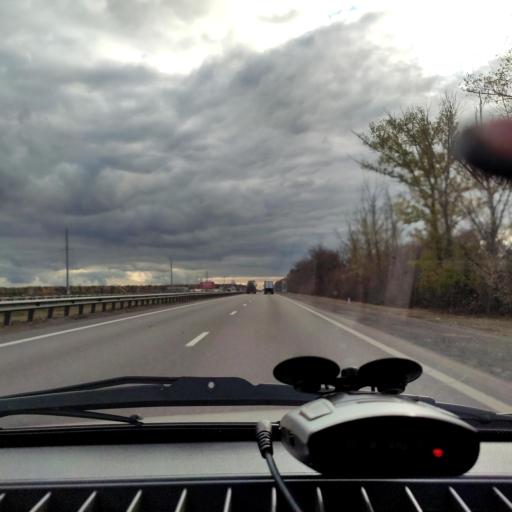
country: RU
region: Voronezj
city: Ramon'
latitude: 51.9123
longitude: 39.2194
